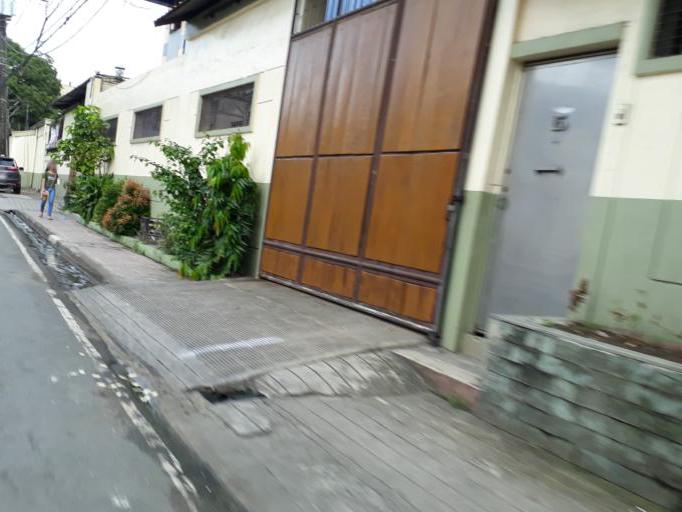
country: PH
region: Calabarzon
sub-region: Province of Rizal
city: Valenzuela
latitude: 14.6818
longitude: 120.9764
